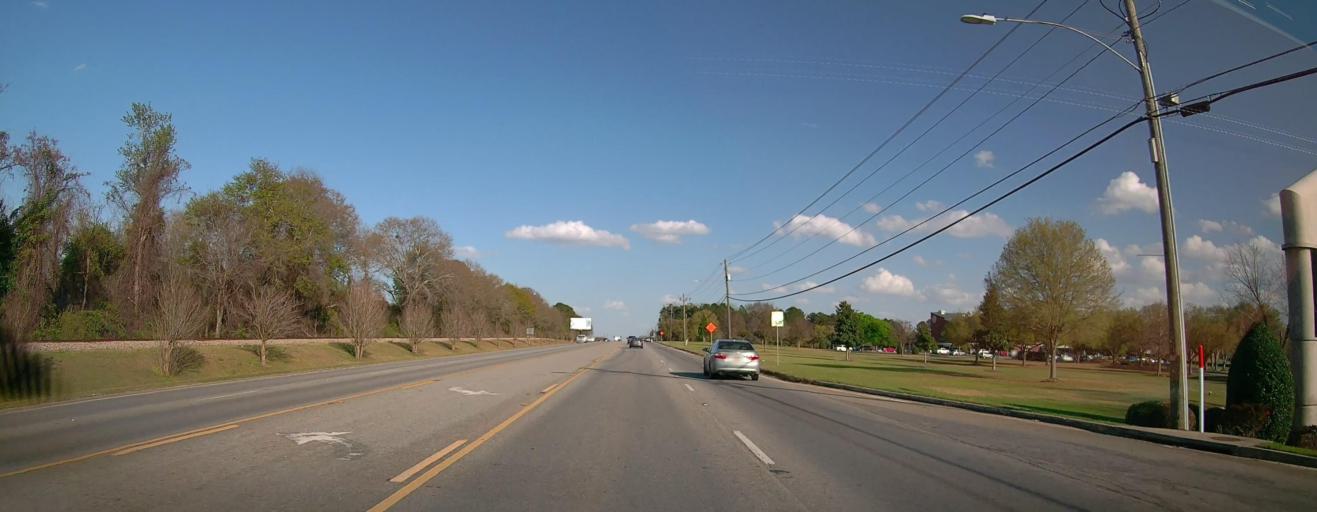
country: US
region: Georgia
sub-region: Toombs County
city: Vidalia
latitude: 32.2058
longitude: -82.3686
